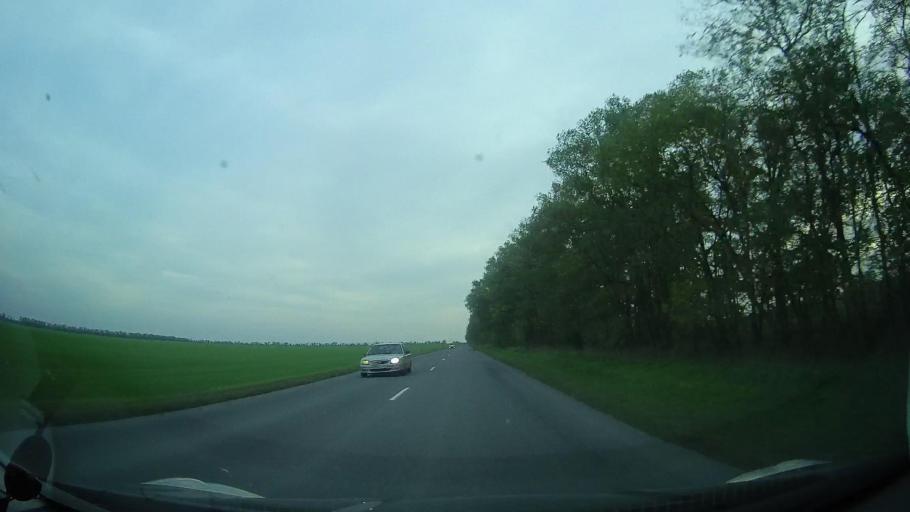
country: RU
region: Rostov
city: Kirovskaya
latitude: 47.0506
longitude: 39.9766
